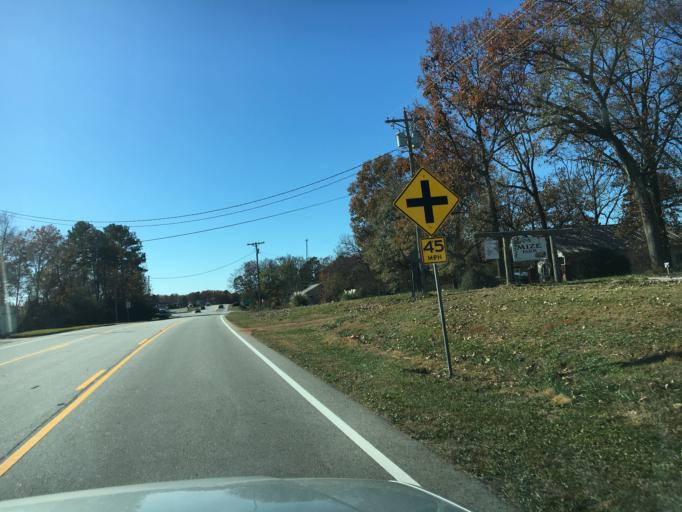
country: US
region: Georgia
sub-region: Hart County
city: Royston
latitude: 34.2912
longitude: -83.0448
